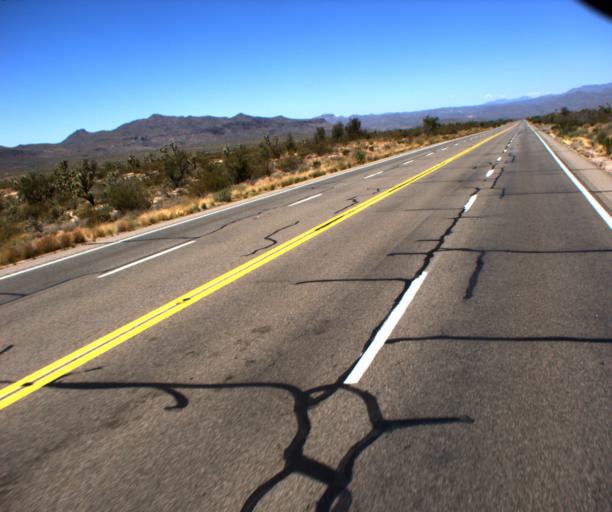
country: US
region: Arizona
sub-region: Yavapai County
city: Congress
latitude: 34.2788
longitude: -113.1009
